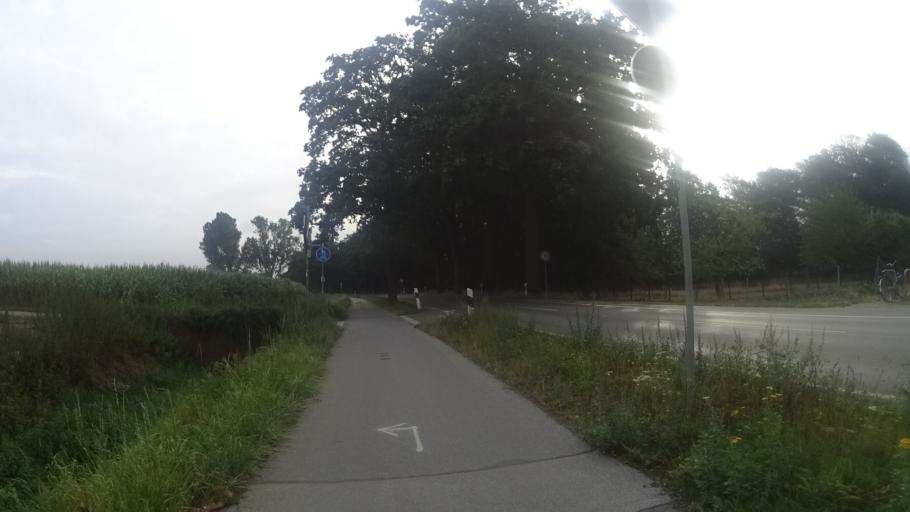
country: DE
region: North Rhine-Westphalia
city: Geldern
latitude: 51.5072
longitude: 6.2774
